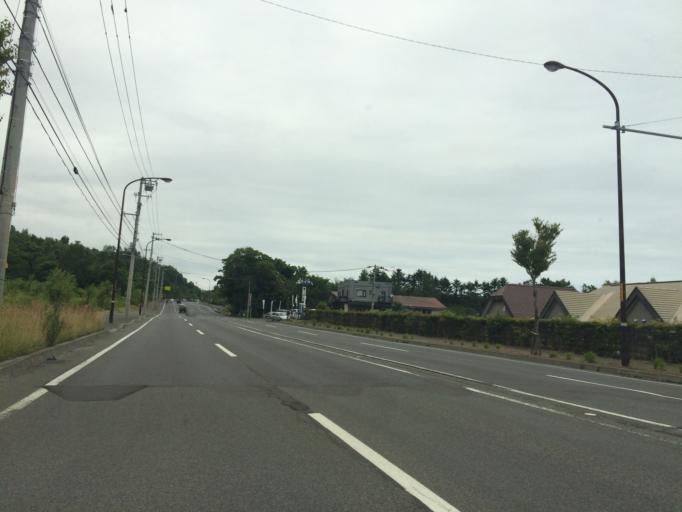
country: JP
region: Hokkaido
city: Otaru
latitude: 43.1450
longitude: 141.1427
